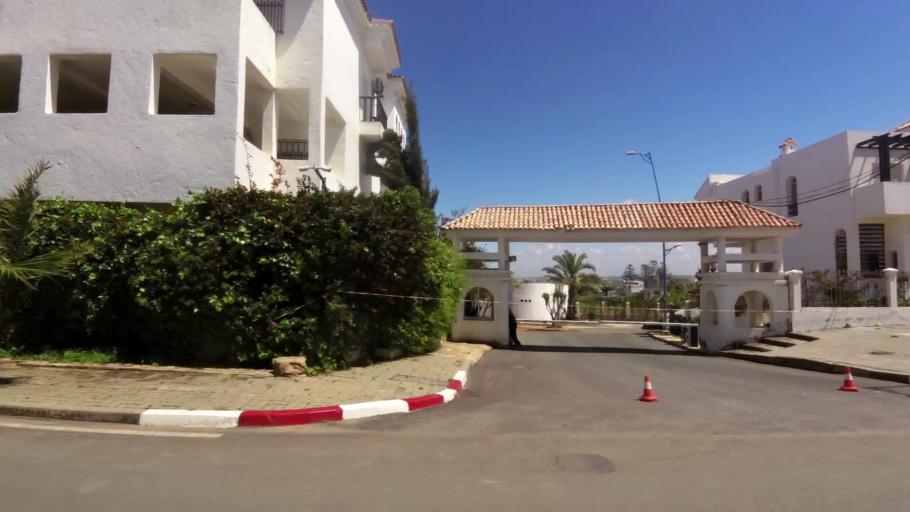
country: MA
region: Grand Casablanca
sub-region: Nouaceur
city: Dar Bouazza
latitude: 33.5271
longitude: -7.8198
